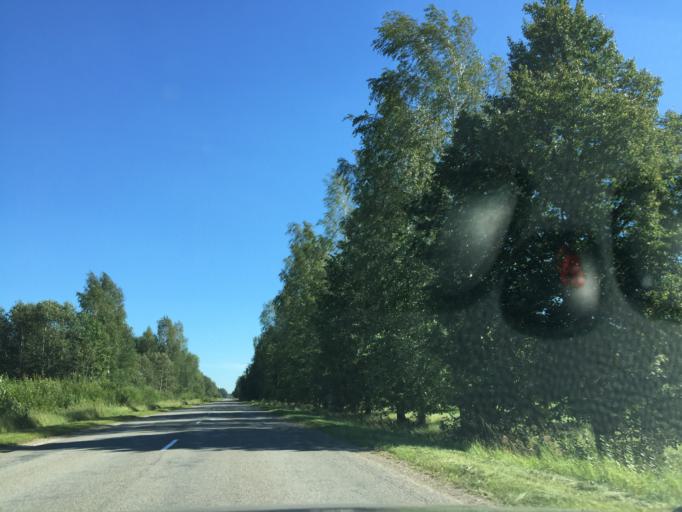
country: LV
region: Akniste
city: Akniste
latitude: 56.1521
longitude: 25.7739
